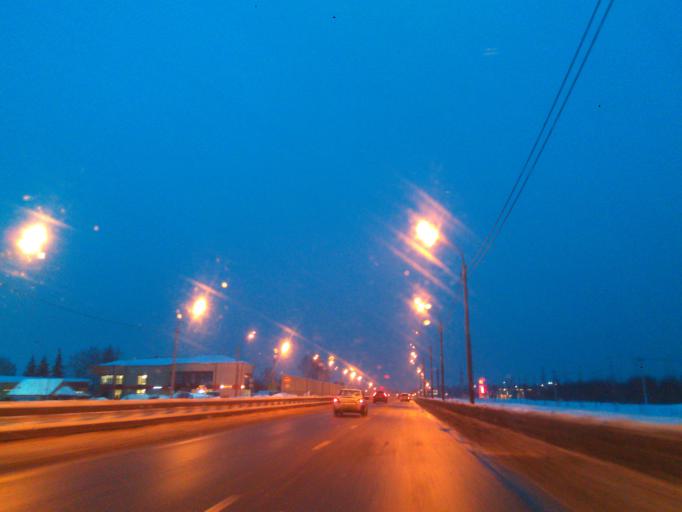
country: RU
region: Moskovskaya
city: Yermolino
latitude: 56.1465
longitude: 37.4906
